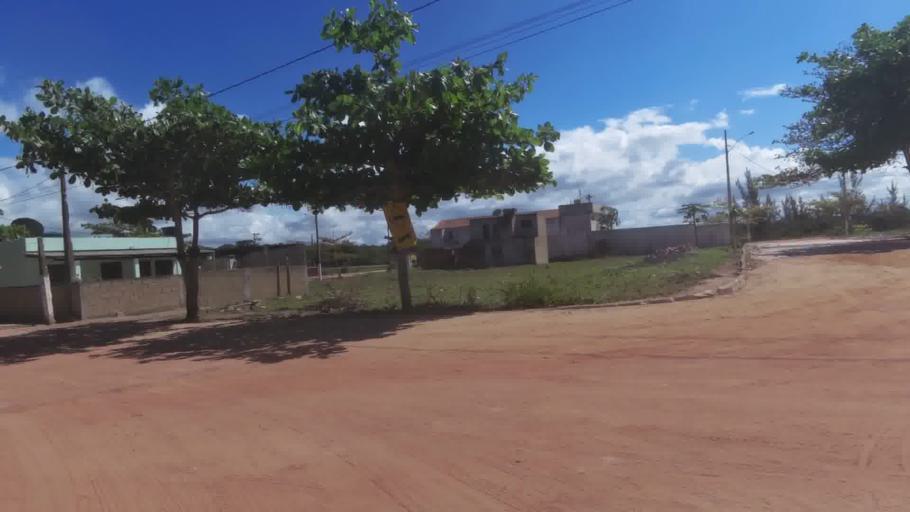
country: BR
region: Espirito Santo
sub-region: Marataizes
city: Marataizes
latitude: -21.2758
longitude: -40.9664
